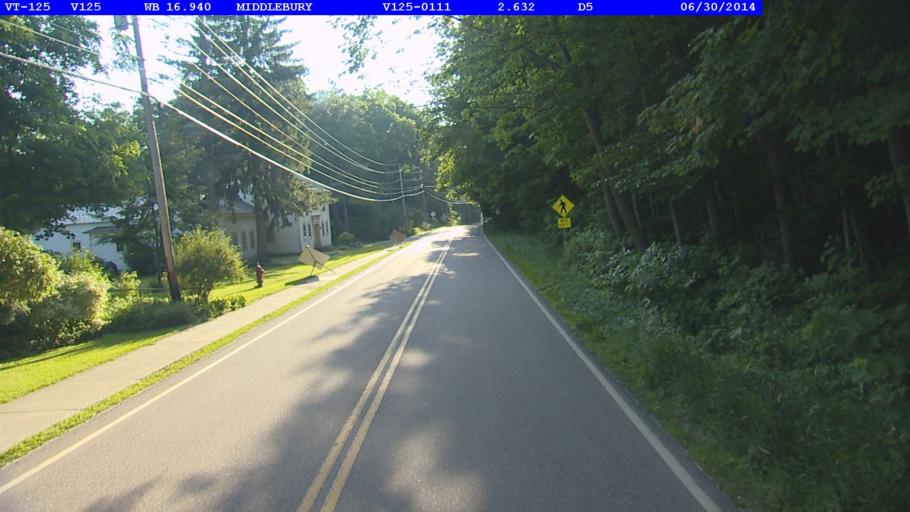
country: US
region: Vermont
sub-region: Addison County
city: Middlebury (village)
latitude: 43.9708
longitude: -73.0895
